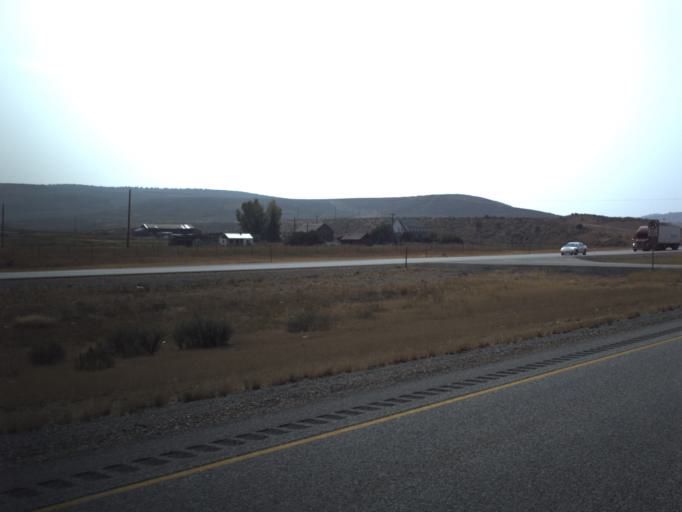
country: US
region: Wyoming
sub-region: Uinta County
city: Evanston
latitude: 41.1228
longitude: -111.1835
